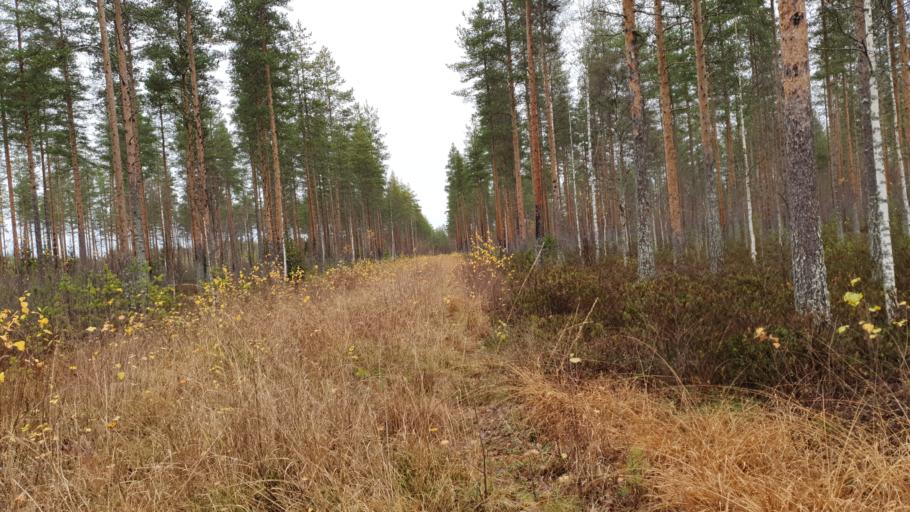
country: FI
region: Kainuu
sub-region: Kehys-Kainuu
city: Kuhmo
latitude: 64.1401
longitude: 29.4172
